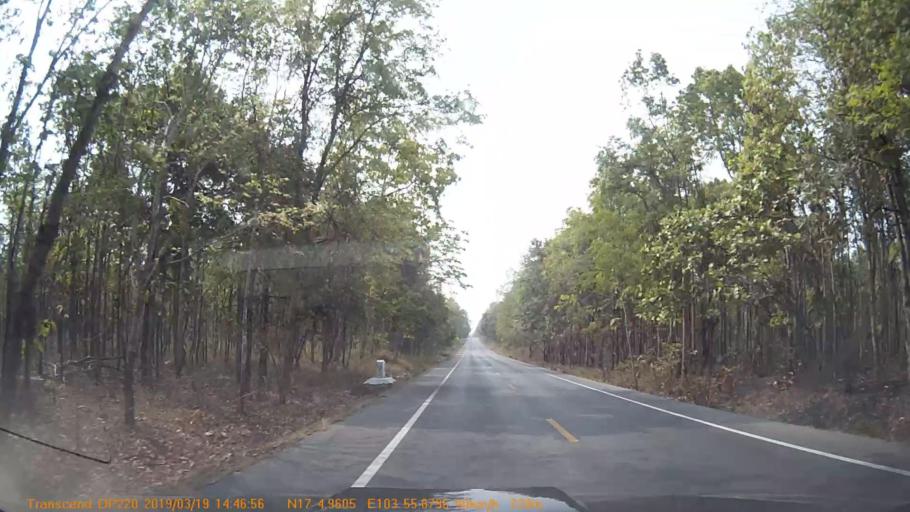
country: TH
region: Sakon Nakhon
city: Phu Phan
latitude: 17.0829
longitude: 103.9311
